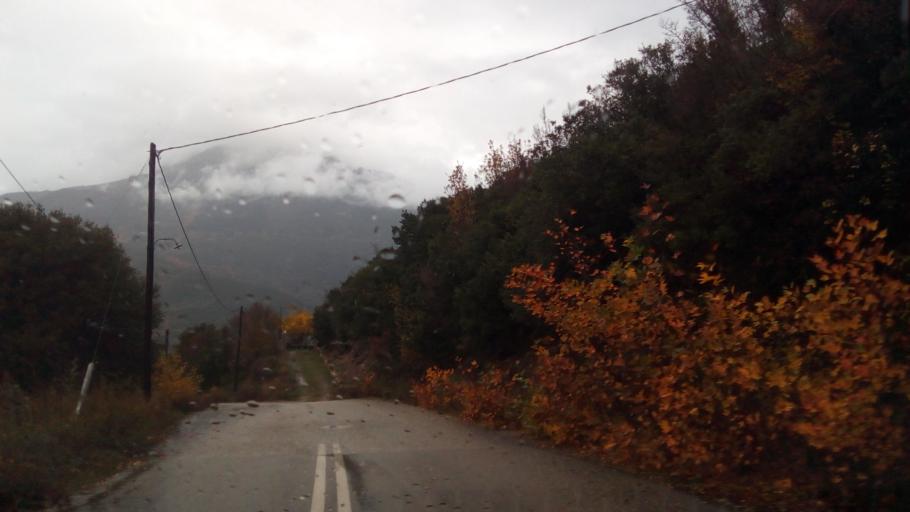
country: GR
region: West Greece
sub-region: Nomos Aitolias kai Akarnanias
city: Thermo
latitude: 38.6551
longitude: 21.8527
